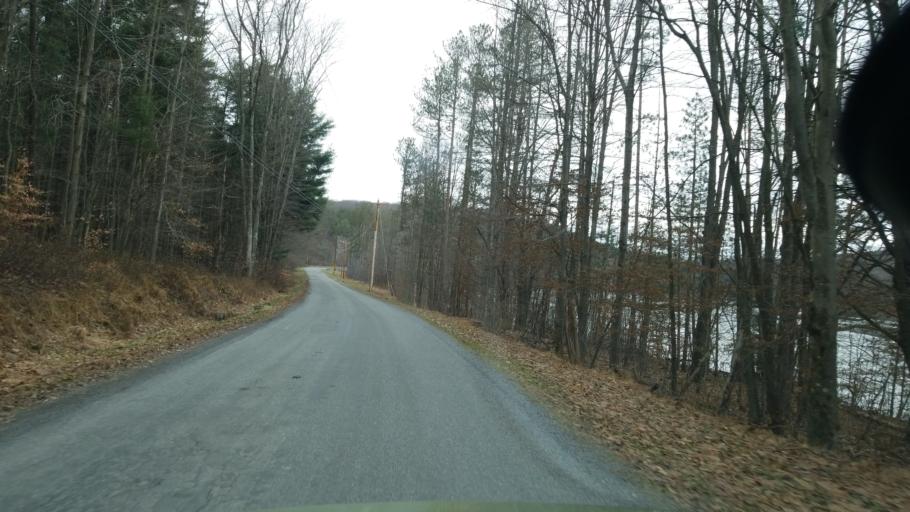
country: US
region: Pennsylvania
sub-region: Clearfield County
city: Treasure Lake
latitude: 41.1102
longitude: -78.6333
